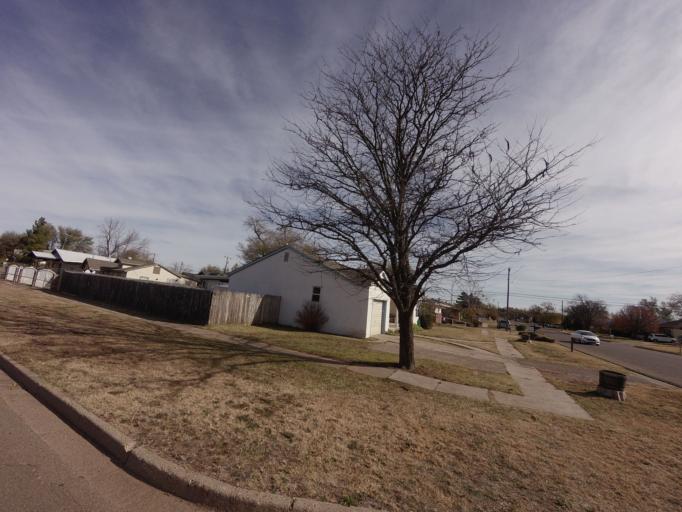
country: US
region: New Mexico
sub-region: Curry County
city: Clovis
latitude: 34.4080
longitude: -103.1952
